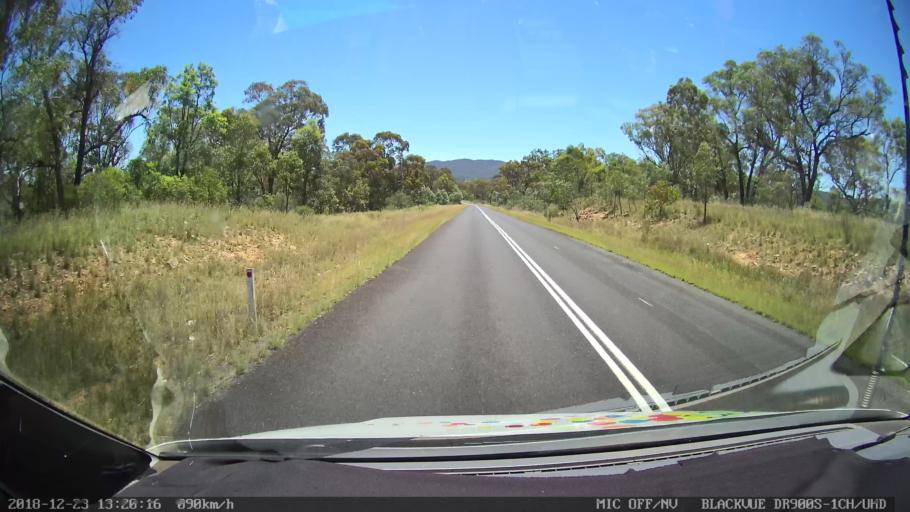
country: AU
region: New South Wales
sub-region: Armidale Dumaresq
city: Armidale
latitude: -30.4856
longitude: 151.4519
